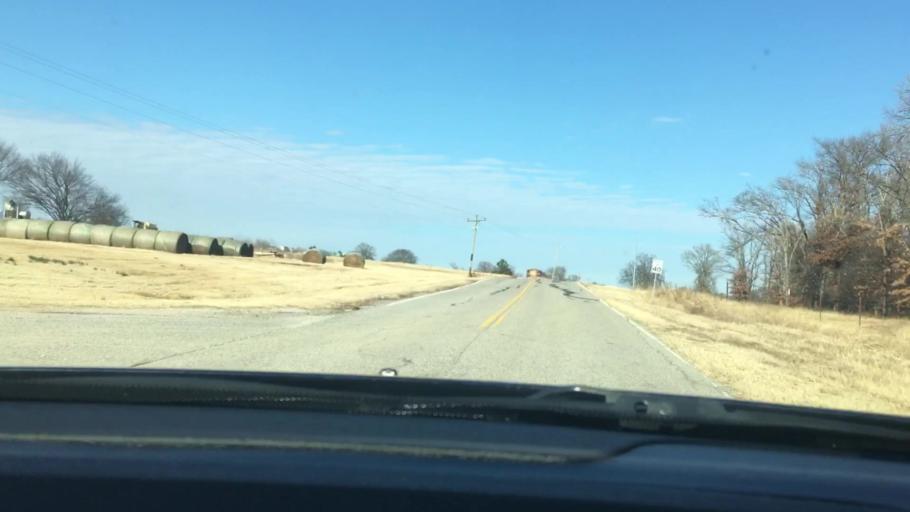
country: US
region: Oklahoma
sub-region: Garvin County
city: Wynnewood
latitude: 34.7240
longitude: -97.1254
